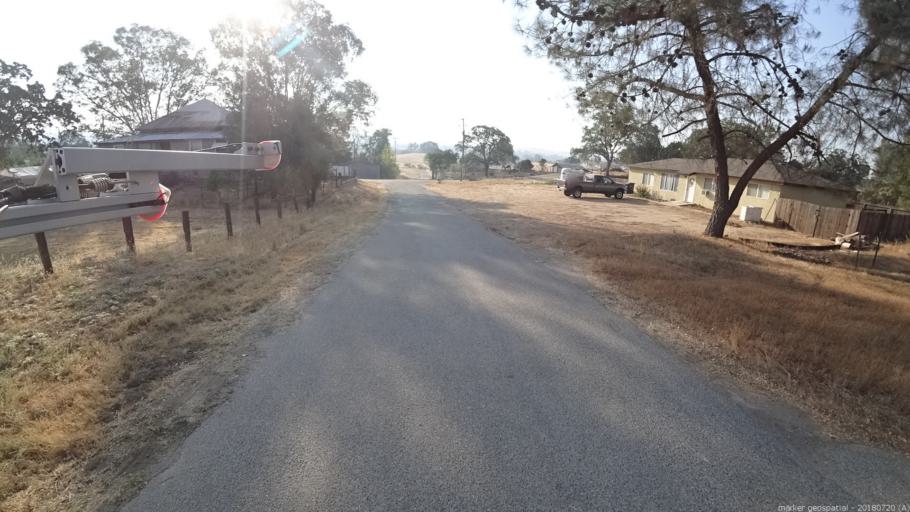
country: US
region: California
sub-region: Madera County
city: Yosemite Lakes
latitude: 37.2121
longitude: -119.9079
